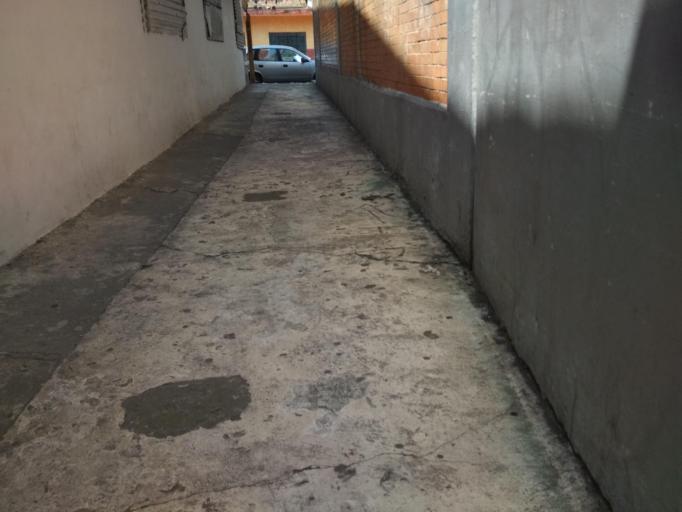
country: MX
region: Veracruz
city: Orizaba
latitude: 18.8406
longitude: -97.1115
